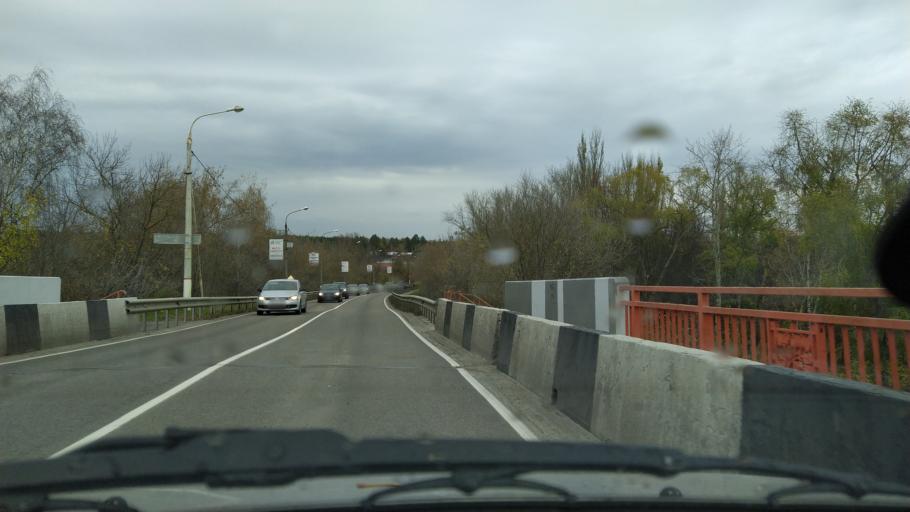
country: RU
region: Moskovskaya
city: Voskresensk
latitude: 55.3224
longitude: 38.6529
